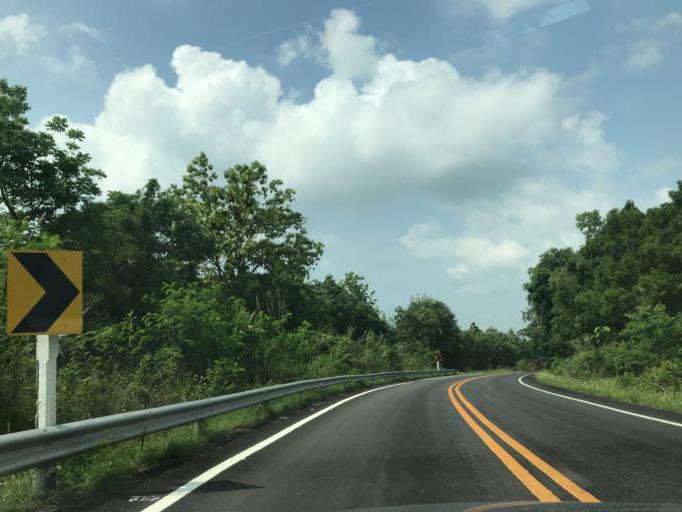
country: TH
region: Phayao
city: Pong
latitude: 19.3125
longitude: 100.3200
